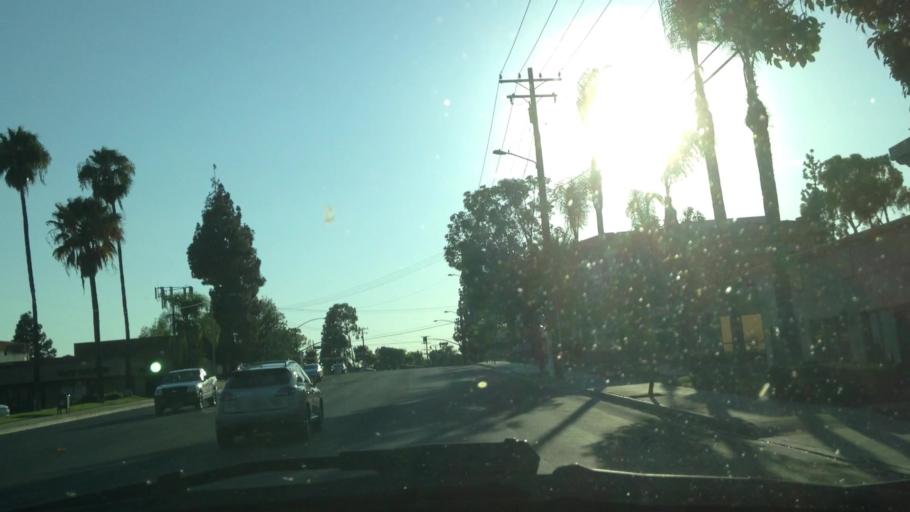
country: US
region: California
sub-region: Orange County
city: Yorba Linda
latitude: 33.8884
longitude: -117.8425
